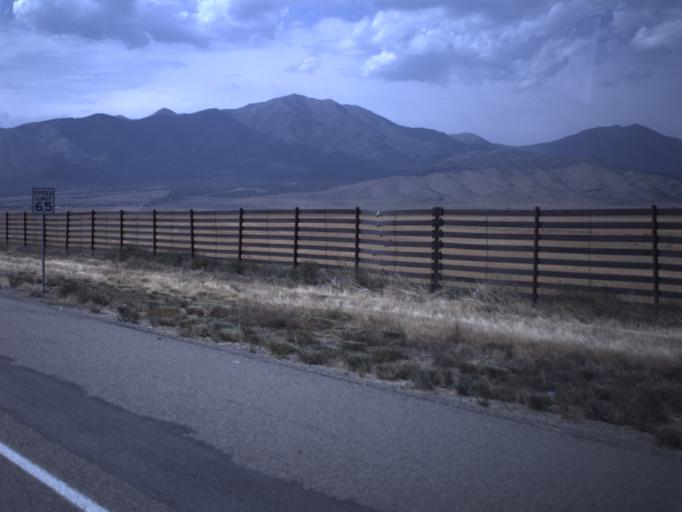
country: US
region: Utah
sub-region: Utah County
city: Eagle Mountain
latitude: 40.3645
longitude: -112.0404
